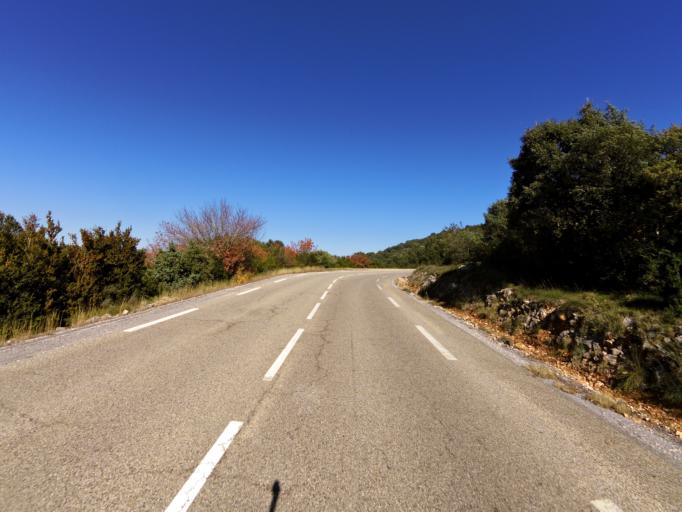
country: FR
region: Rhone-Alpes
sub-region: Departement de l'Ardeche
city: Ruoms
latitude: 44.4055
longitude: 4.4172
